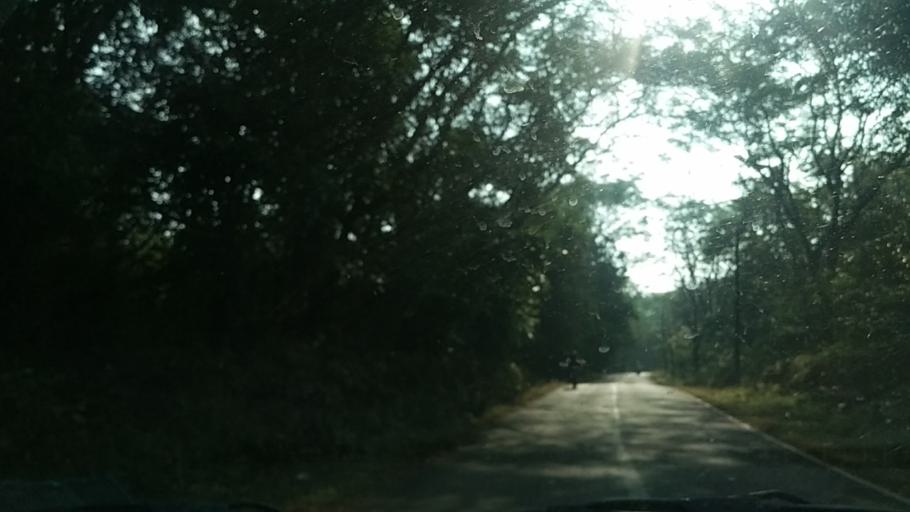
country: IN
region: Goa
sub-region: South Goa
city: Sanguem
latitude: 15.2188
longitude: 74.1993
